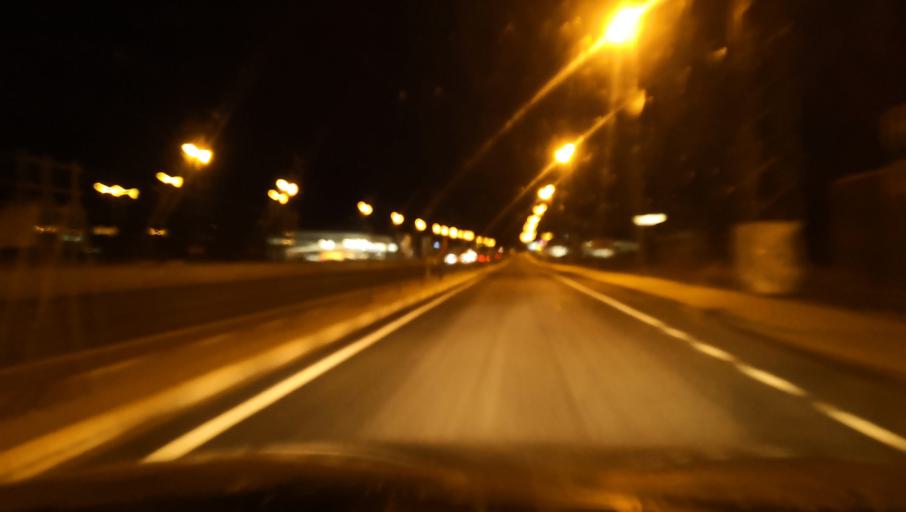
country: ES
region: Castille and Leon
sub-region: Provincia de Zamora
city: Zamora
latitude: 41.5253
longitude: -5.7573
